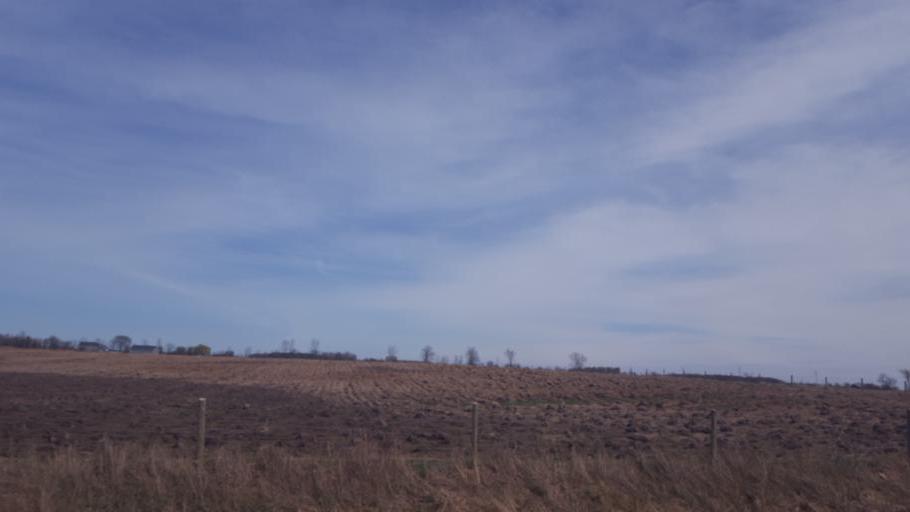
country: US
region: Michigan
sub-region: Gladwin County
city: Gladwin
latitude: 44.0385
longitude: -84.4673
